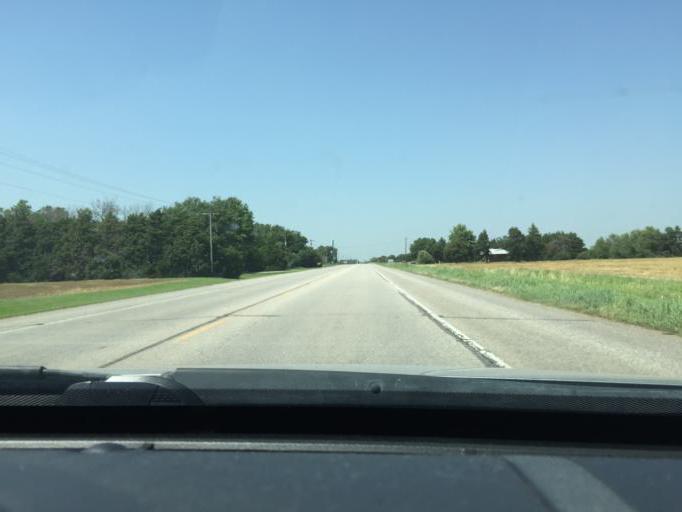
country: US
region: Kansas
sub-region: Reno County
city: Haven
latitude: 37.9465
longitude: -97.8668
